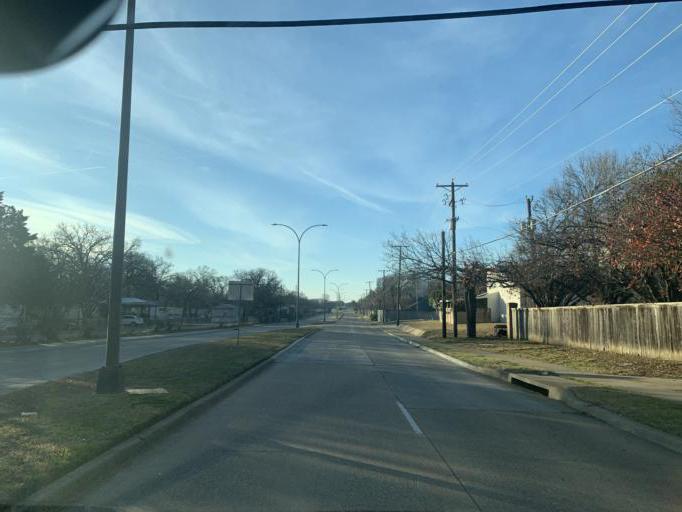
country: US
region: Texas
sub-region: Tarrant County
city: Arlington
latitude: 32.7720
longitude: -97.0738
